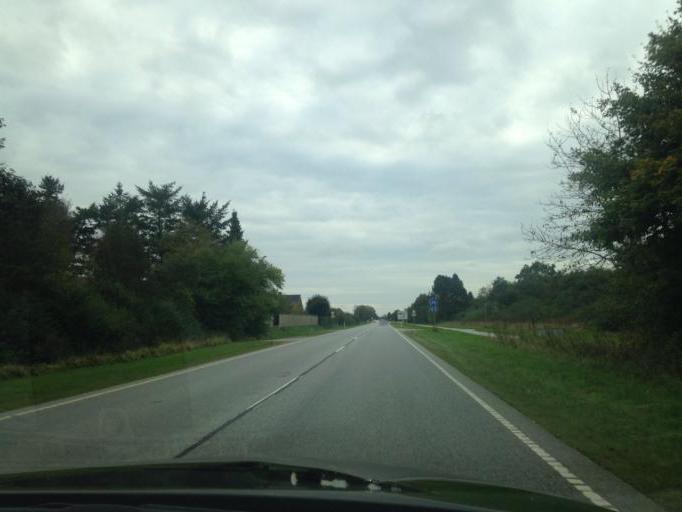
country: DK
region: South Denmark
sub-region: Haderslev Kommune
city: Vojens
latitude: 55.2536
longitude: 9.3494
